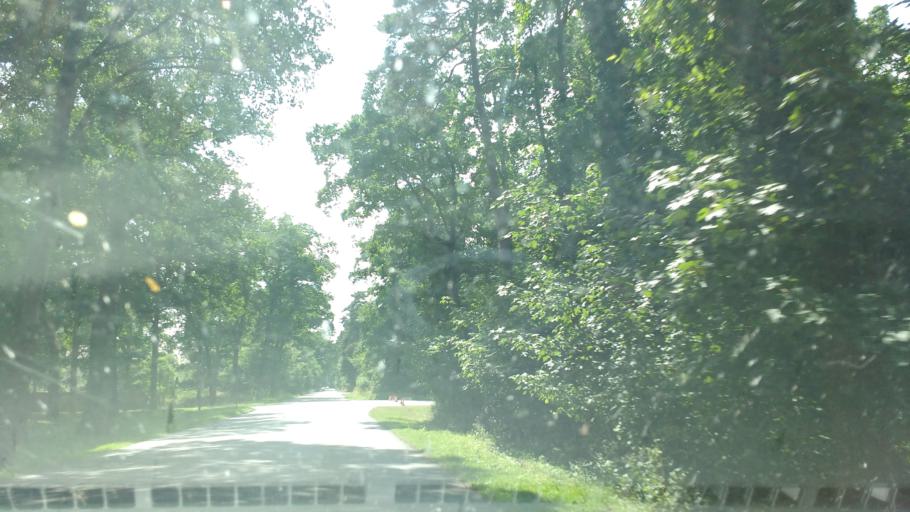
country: DE
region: North Rhine-Westphalia
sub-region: Regierungsbezirk Detmold
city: Paderborn
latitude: 51.7744
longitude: 8.7316
